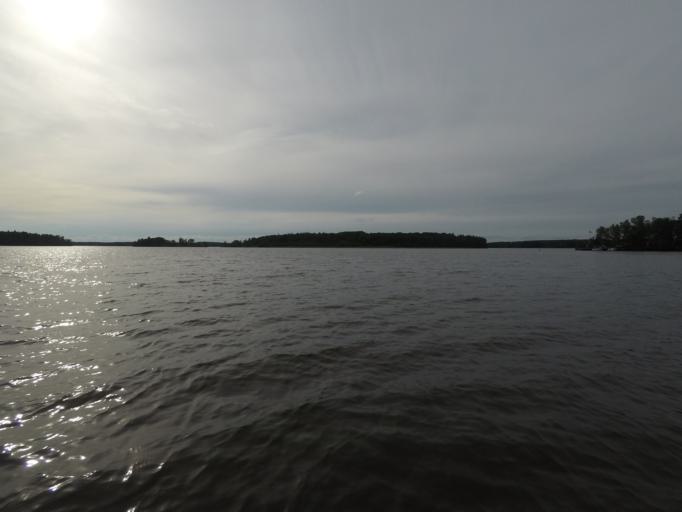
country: SE
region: Soedermanland
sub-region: Eskilstuna Kommun
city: Torshalla
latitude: 59.4792
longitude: 16.4181
